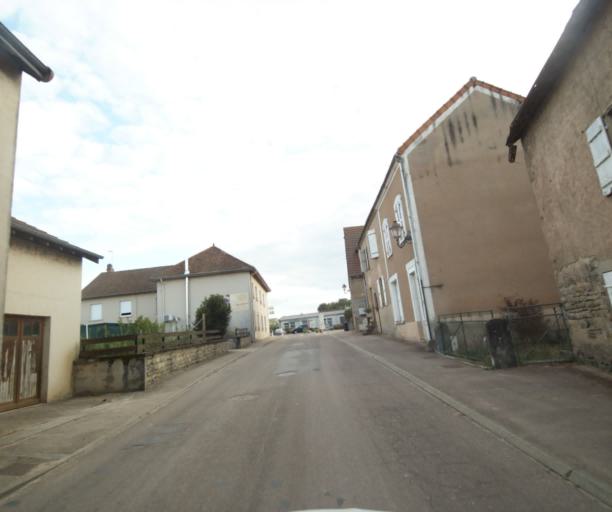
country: FR
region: Bourgogne
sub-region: Departement de Saone-et-Loire
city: Charolles
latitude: 46.4418
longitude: 4.3377
